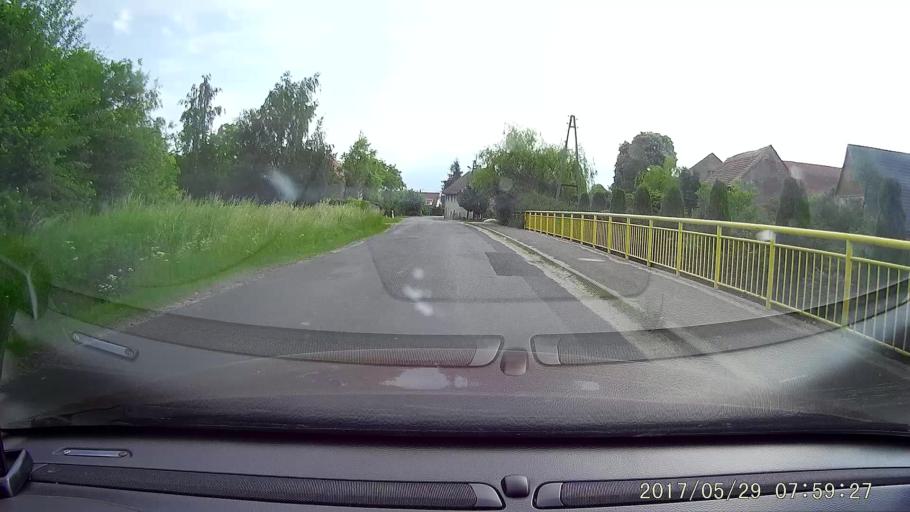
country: PL
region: Lower Silesian Voivodeship
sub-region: Powiat zlotoryjski
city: Olszanica
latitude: 51.2049
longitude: 15.7967
